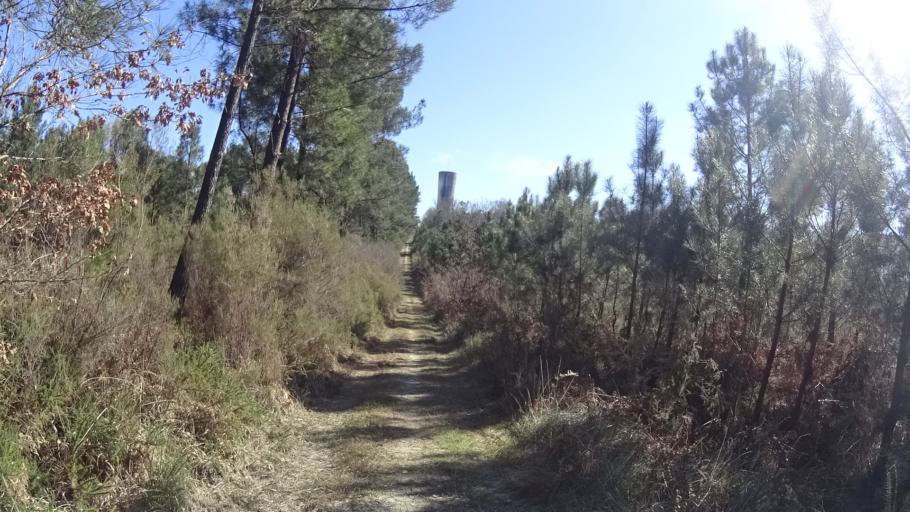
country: FR
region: Aquitaine
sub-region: Departement de la Dordogne
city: Saint-Aulaye
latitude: 45.1317
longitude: 0.2123
